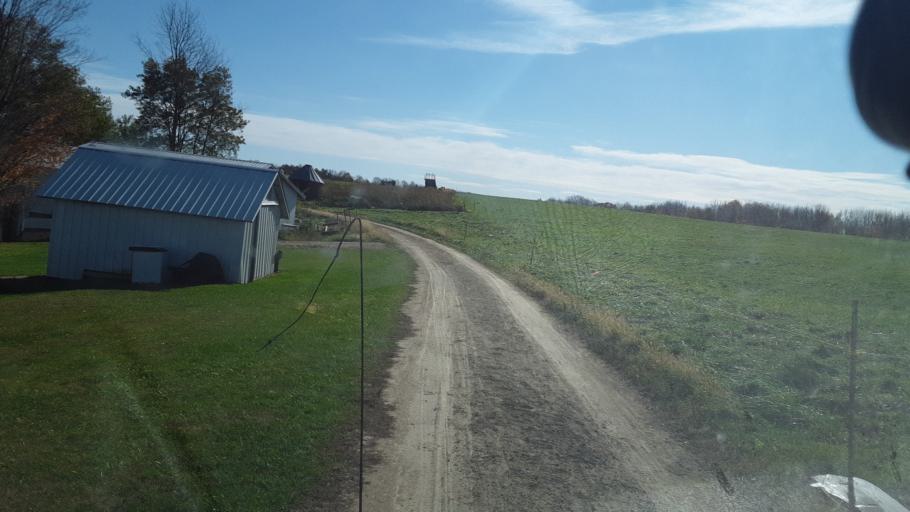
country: US
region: Wisconsin
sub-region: Vernon County
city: Hillsboro
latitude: 43.6862
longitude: -90.4097
